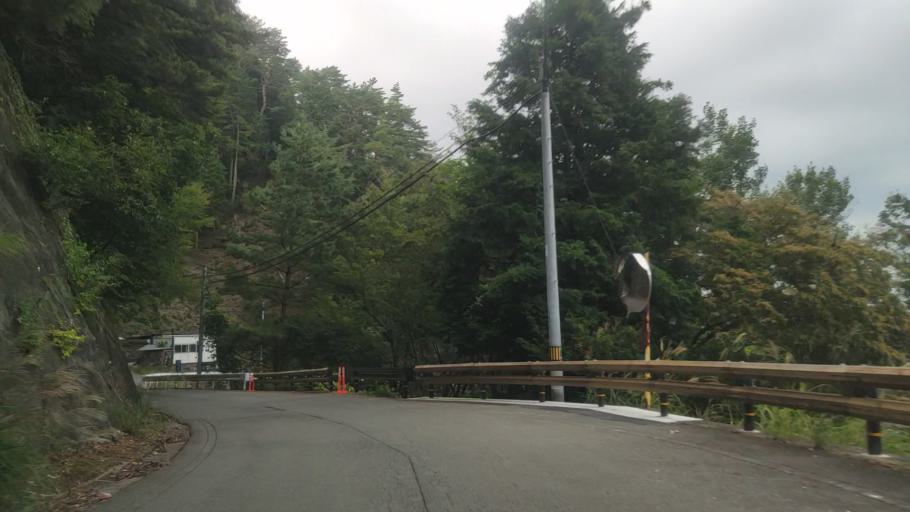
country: JP
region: Wakayama
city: Koya
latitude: 34.2207
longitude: 135.6131
